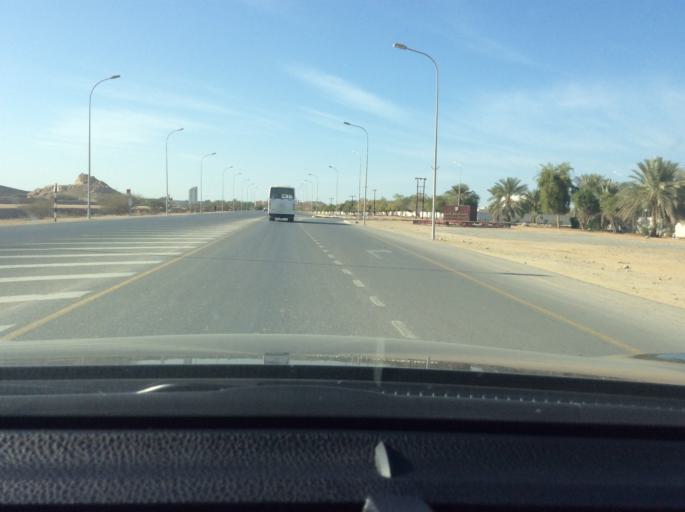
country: OM
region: Muhafazat Masqat
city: As Sib al Jadidah
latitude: 23.5799
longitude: 58.1762
